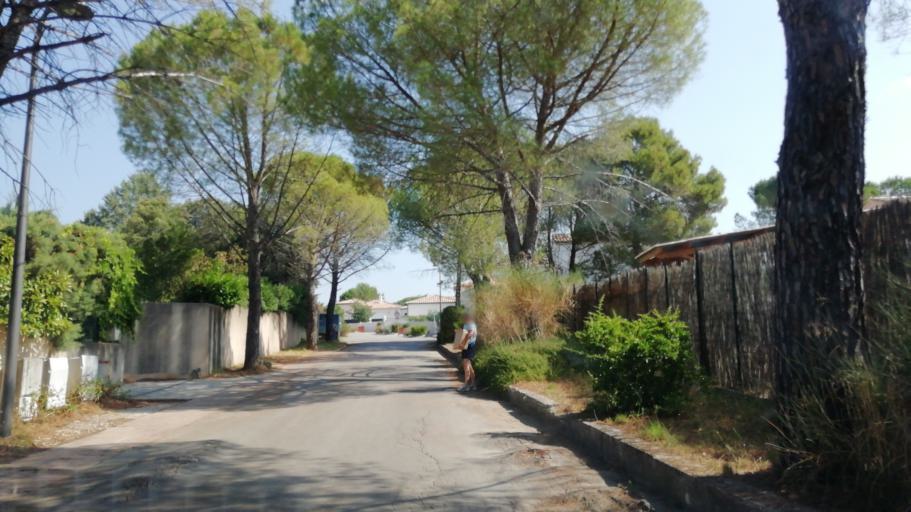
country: FR
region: Languedoc-Roussillon
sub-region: Departement de l'Herault
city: Saint-Mathieu-de-Treviers
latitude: 43.7422
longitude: 3.8568
